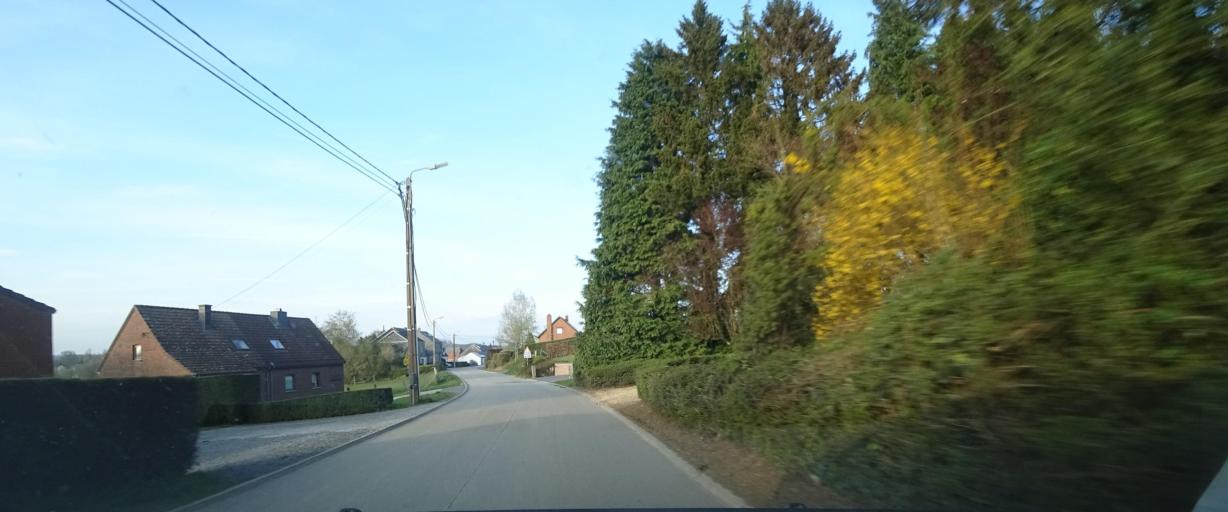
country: BE
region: Wallonia
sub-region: Province de Namur
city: Hamois
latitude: 50.3132
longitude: 5.1470
